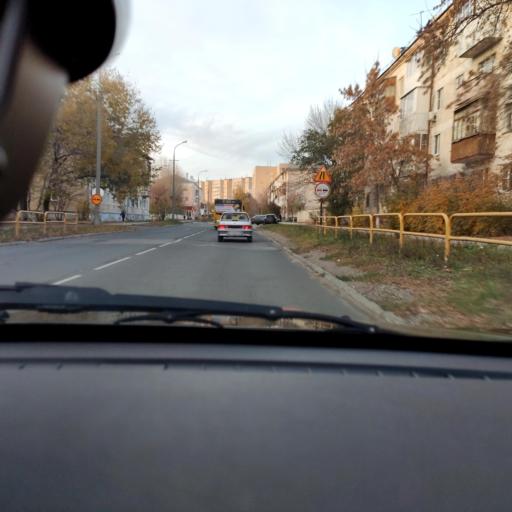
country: RU
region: Samara
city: Tol'yatti
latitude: 53.5044
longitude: 49.4002
